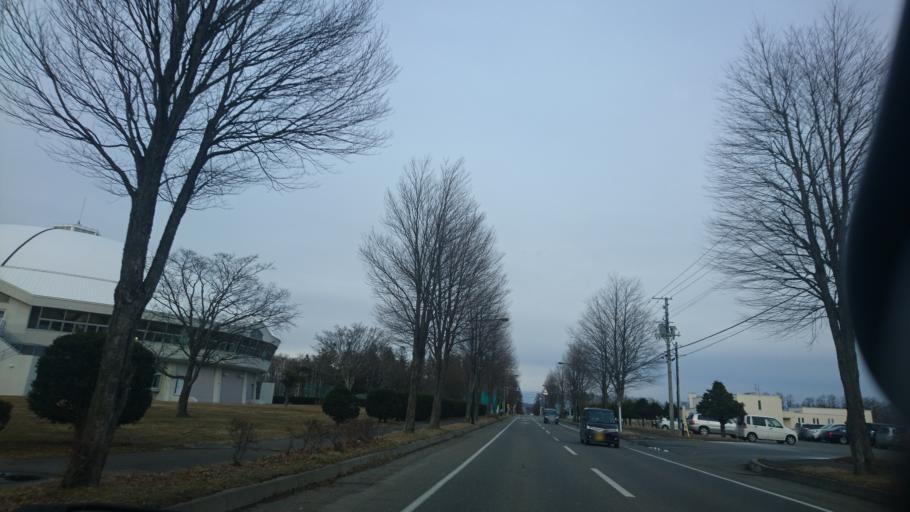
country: JP
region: Hokkaido
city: Otofuke
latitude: 42.9916
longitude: 143.1931
